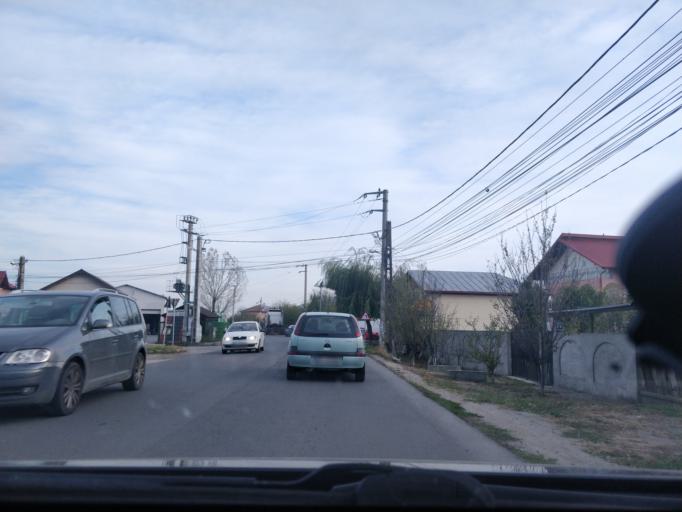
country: RO
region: Giurgiu
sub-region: Comuna Bolintin Vale
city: Malu Spart
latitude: 44.4346
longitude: 25.7228
